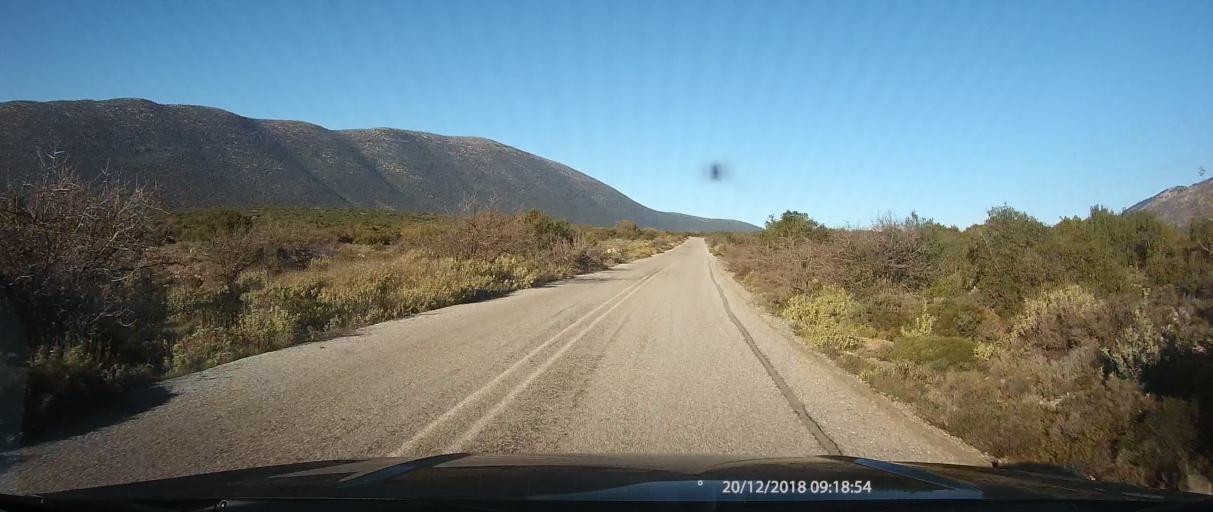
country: GR
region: Peloponnese
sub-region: Nomos Lakonias
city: Molaoi
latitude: 36.9146
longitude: 22.9482
